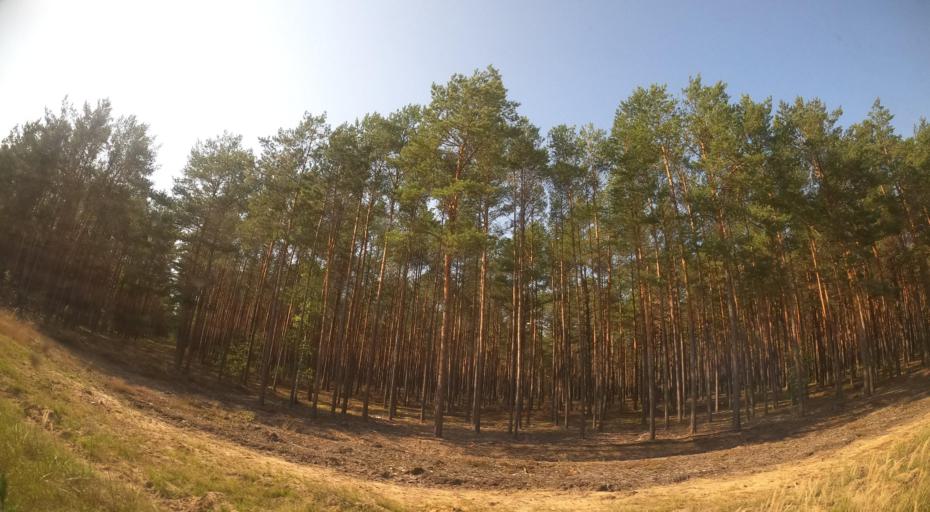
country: PL
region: Lubusz
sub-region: Powiat zielonogorski
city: Nowogrod Bobrzanski
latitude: 51.8274
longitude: 15.2546
